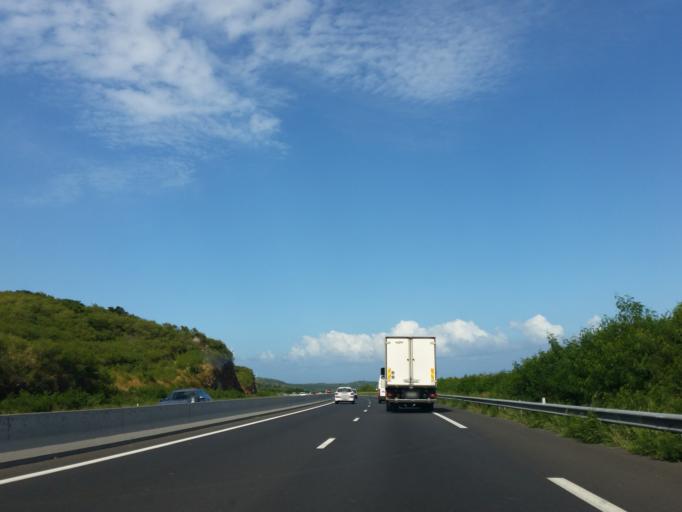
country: RE
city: Piton Saint-Leu
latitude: -21.2420
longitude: 55.3169
